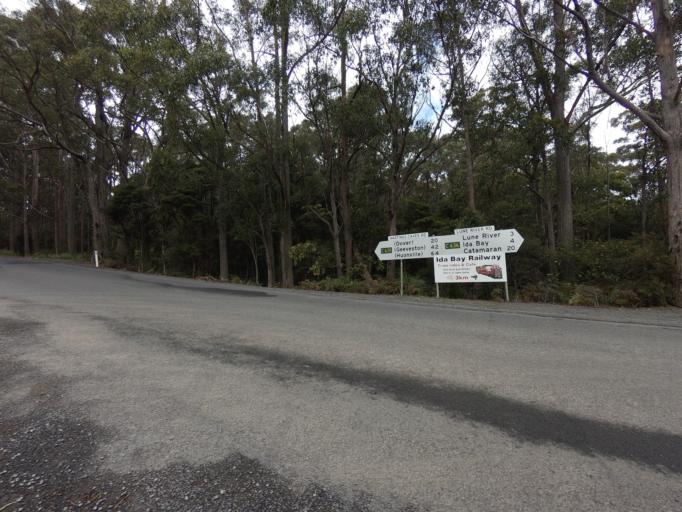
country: AU
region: Tasmania
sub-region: Huon Valley
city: Geeveston
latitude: -43.4164
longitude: 146.9092
